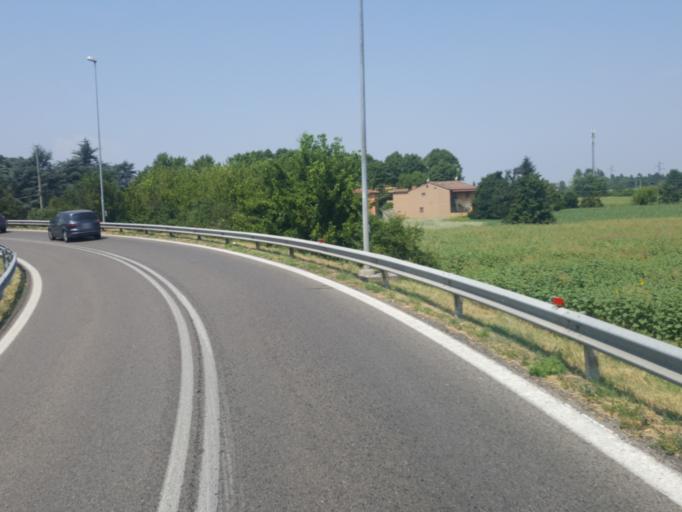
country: IT
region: Emilia-Romagna
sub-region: Provincia di Bologna
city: Calderara di Reno
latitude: 44.5279
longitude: 11.2498
